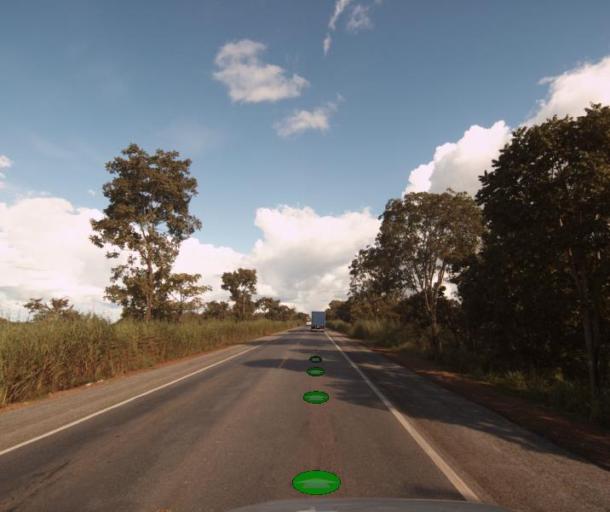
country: BR
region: Goias
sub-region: Porangatu
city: Porangatu
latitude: -13.1381
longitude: -49.1901
